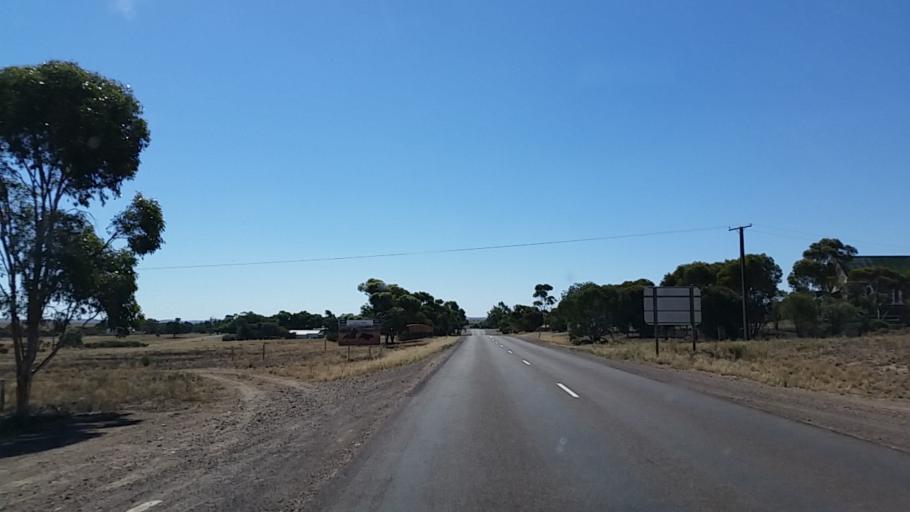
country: AU
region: South Australia
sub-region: Flinders Ranges
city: Quorn
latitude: -32.4282
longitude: 138.5312
